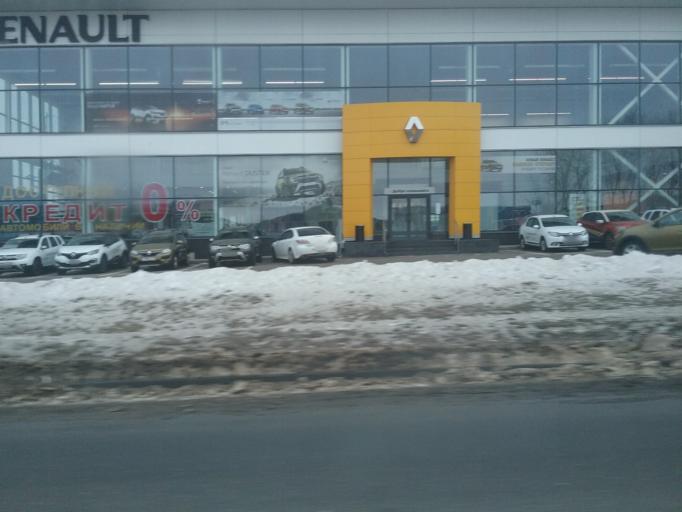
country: RU
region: Tula
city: Tula
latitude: 54.1597
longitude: 37.6370
